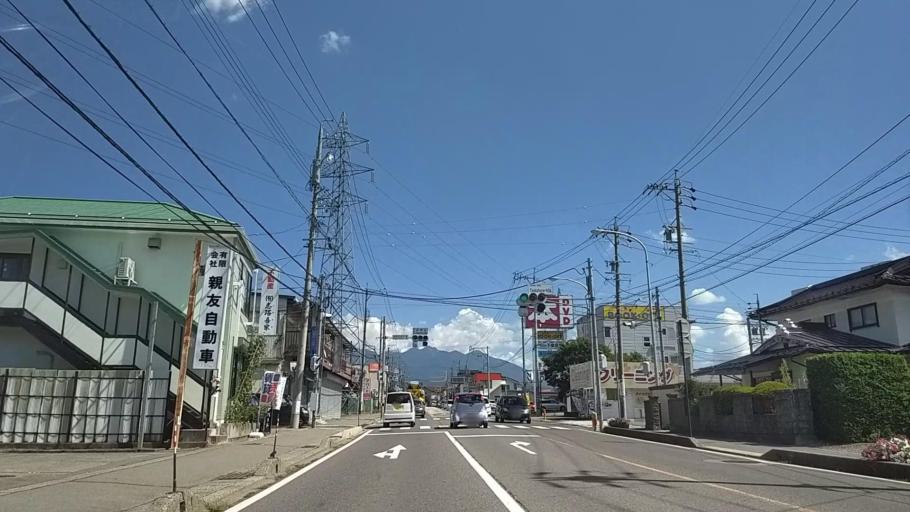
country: JP
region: Nagano
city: Chino
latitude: 35.9991
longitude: 138.1569
